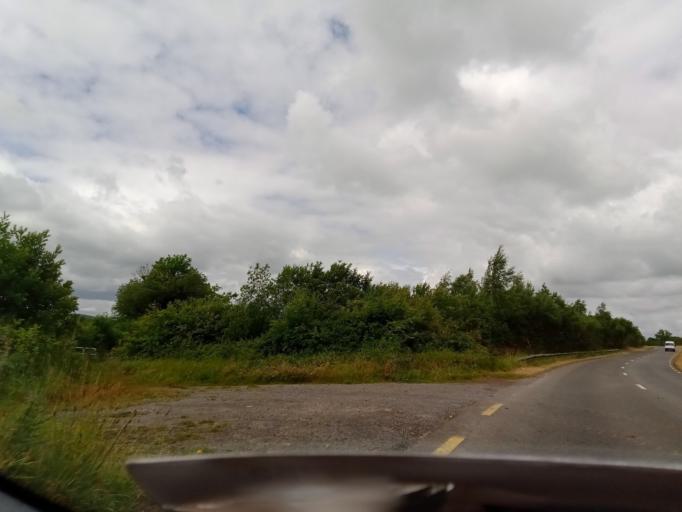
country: IE
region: Leinster
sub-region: Kilkenny
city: Thomastown
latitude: 52.4849
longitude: -7.2229
